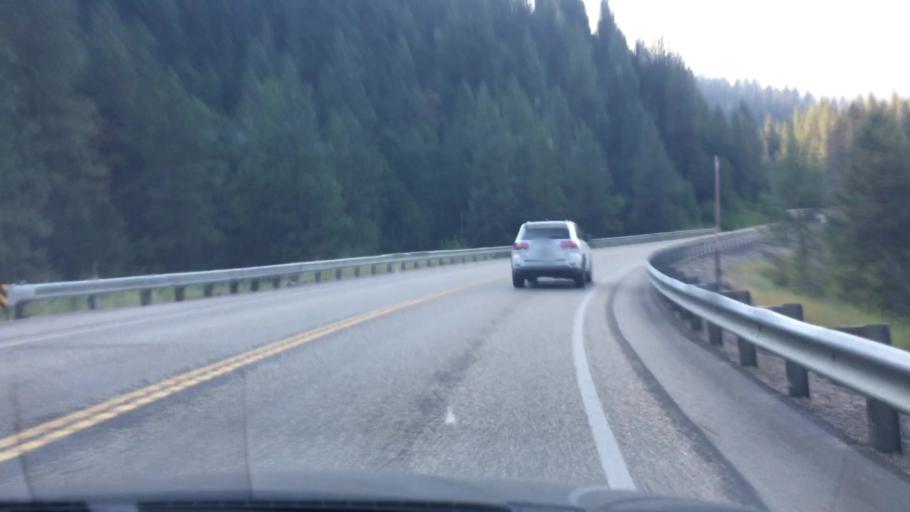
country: US
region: Idaho
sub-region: Valley County
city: Cascade
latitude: 44.1514
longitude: -116.1138
